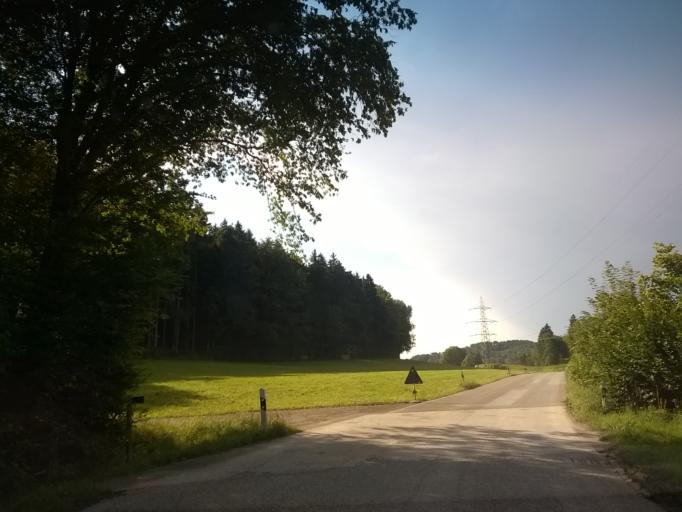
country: CH
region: Zurich
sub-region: Bezirk Buelach
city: Birchwil
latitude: 47.4819
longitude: 8.6342
